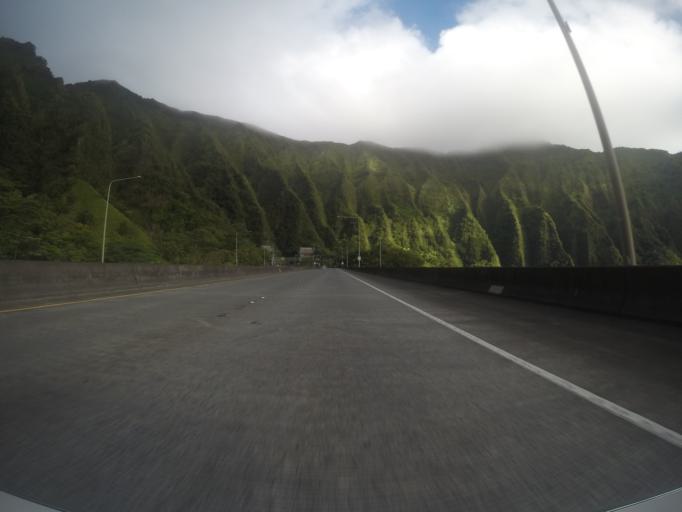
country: US
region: Hawaii
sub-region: Honolulu County
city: Kane'ohe
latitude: 21.4027
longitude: -157.8309
